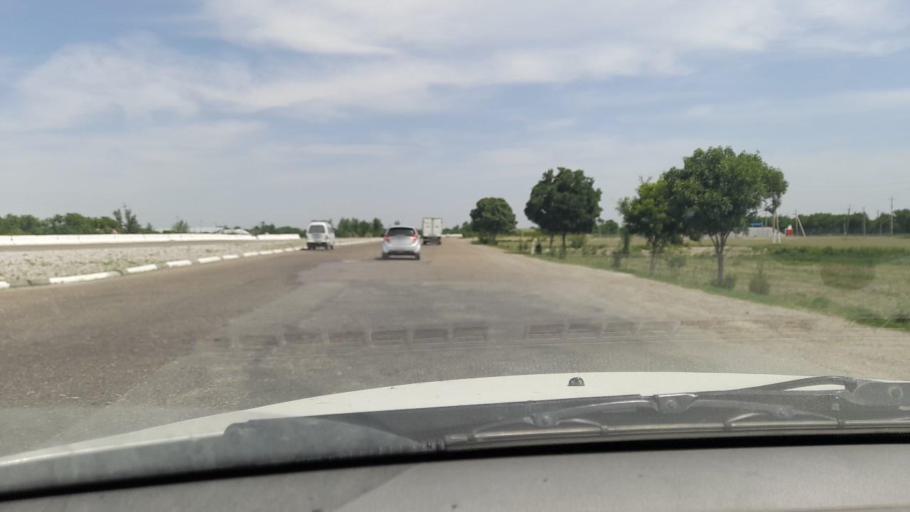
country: UZ
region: Bukhara
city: Wobkent
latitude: 40.0523
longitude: 64.5391
